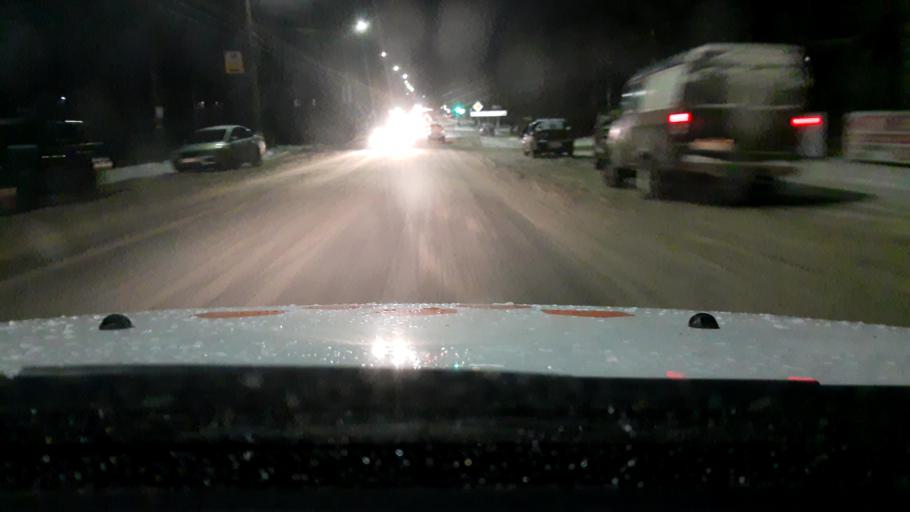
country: RU
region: Nizjnij Novgorod
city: Gorodets
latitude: 56.6681
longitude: 43.4672
